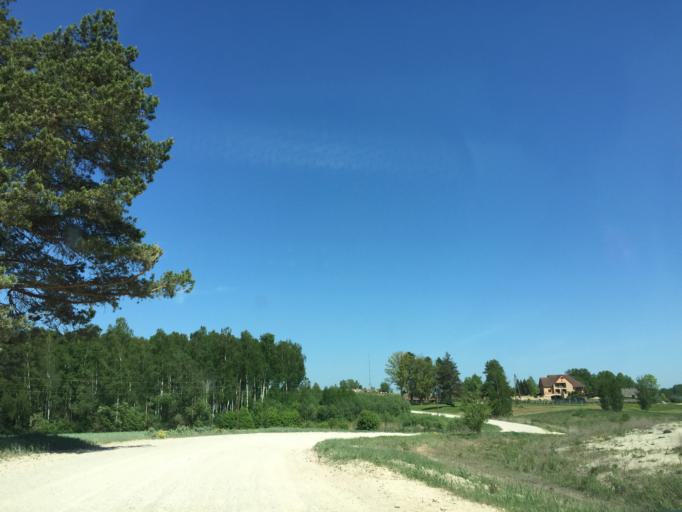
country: LV
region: Ikskile
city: Ikskile
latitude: 56.8620
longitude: 24.5005
